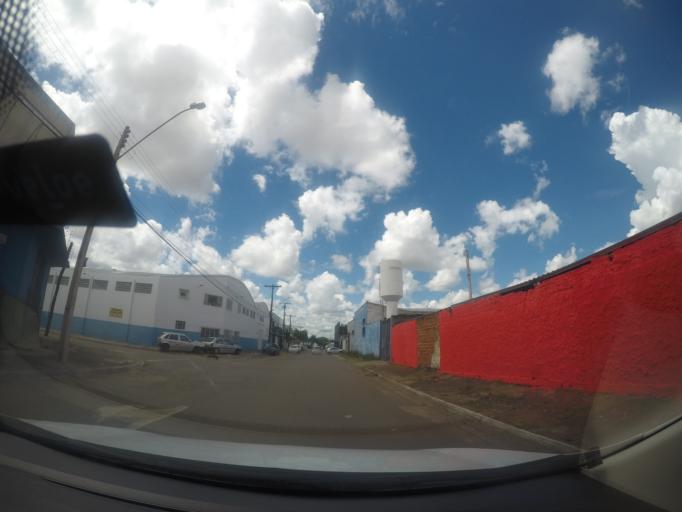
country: BR
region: Goias
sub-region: Goiania
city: Goiania
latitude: -16.6650
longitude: -49.3063
